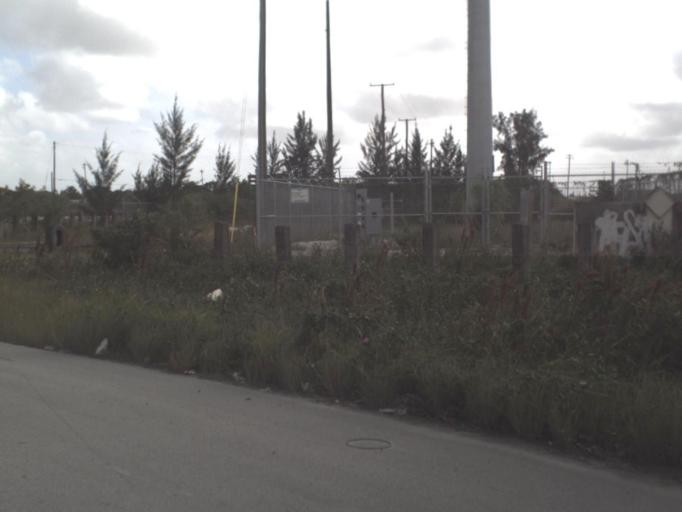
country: US
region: Florida
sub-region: Miami-Dade County
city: Miami Springs
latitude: 25.8393
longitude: -80.3095
